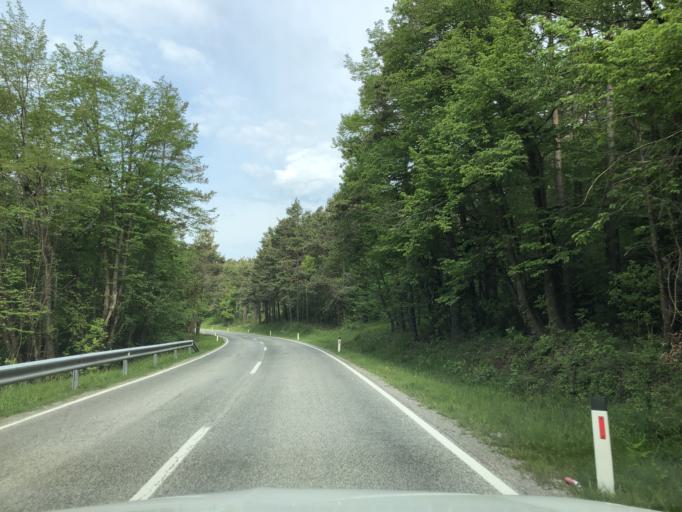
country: SI
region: Bloke
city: Nova Vas
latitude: 45.7639
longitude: 14.4763
